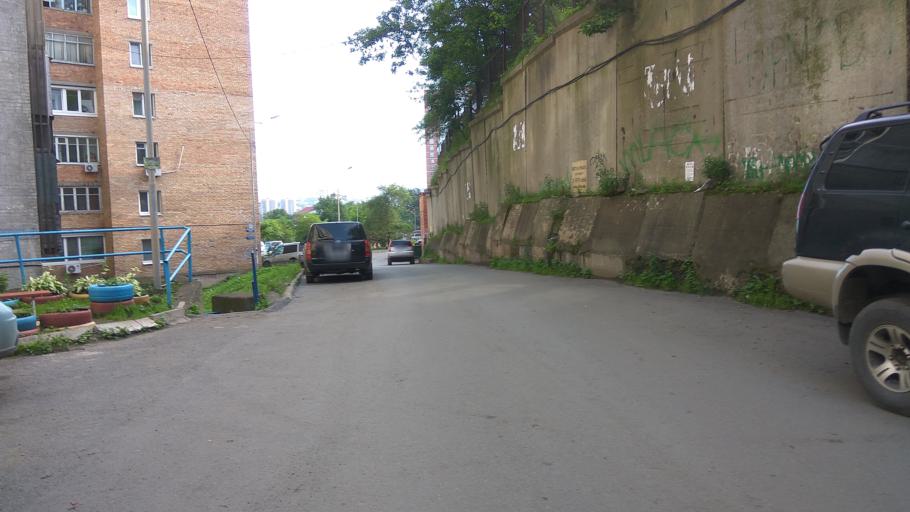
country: RU
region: Primorskiy
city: Vladivostok
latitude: 43.1183
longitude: 131.9365
